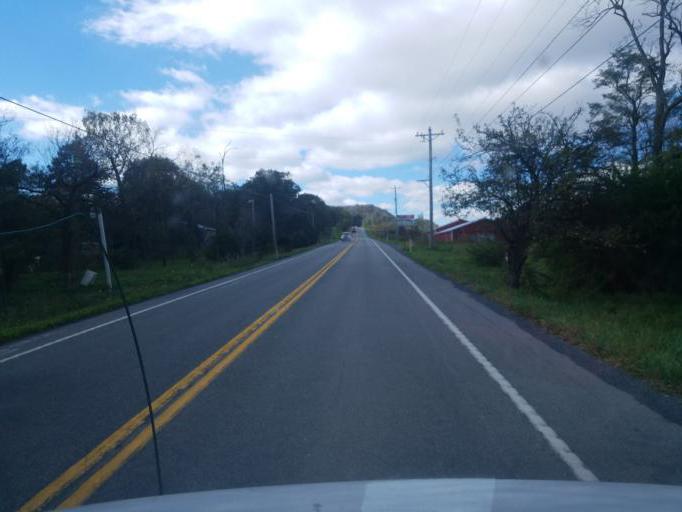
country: US
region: Pennsylvania
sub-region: Bedford County
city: Earlston
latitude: 40.0184
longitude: -78.1891
